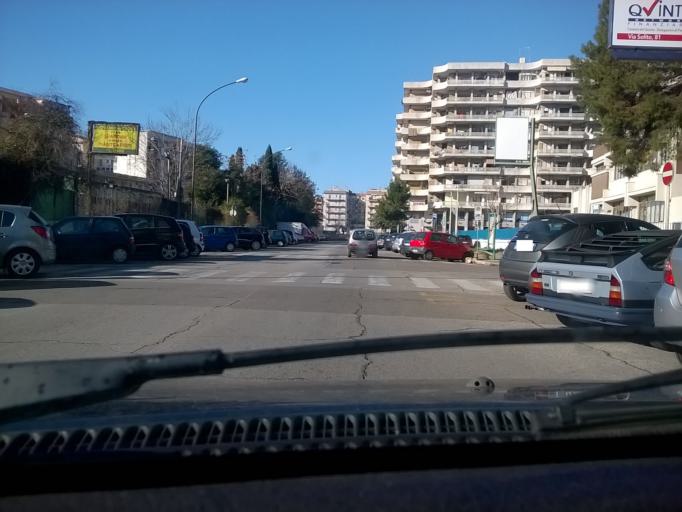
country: IT
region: Apulia
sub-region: Provincia di Taranto
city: Taranto
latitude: 40.4613
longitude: 17.2619
